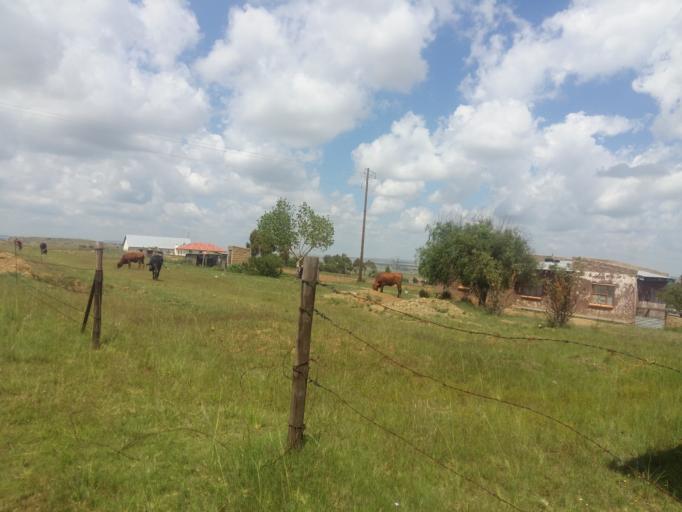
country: LS
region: Mafeteng
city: Mafeteng
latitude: -29.7541
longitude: 27.1153
